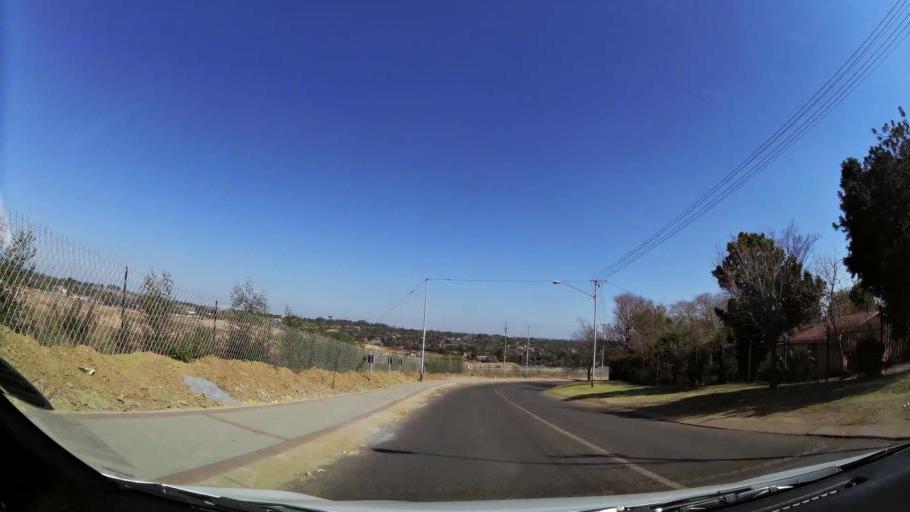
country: ZA
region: Gauteng
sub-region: City of Tshwane Metropolitan Municipality
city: Centurion
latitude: -25.8038
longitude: 28.2386
